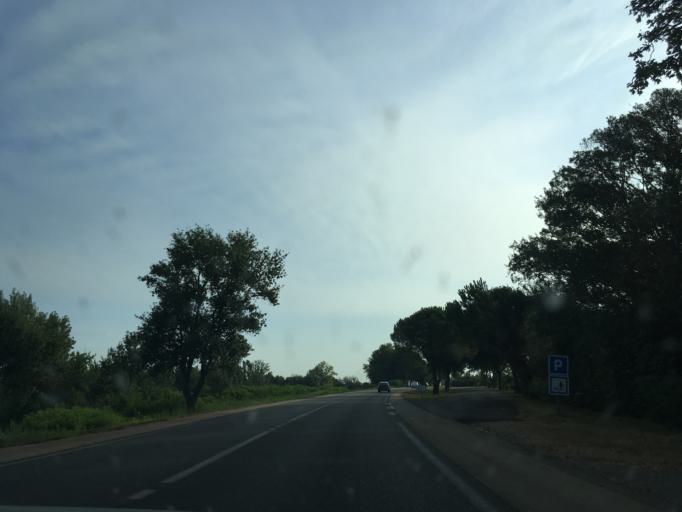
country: FR
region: Languedoc-Roussillon
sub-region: Departement du Gard
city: Saint-Gilles
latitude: 43.6138
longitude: 4.4804
